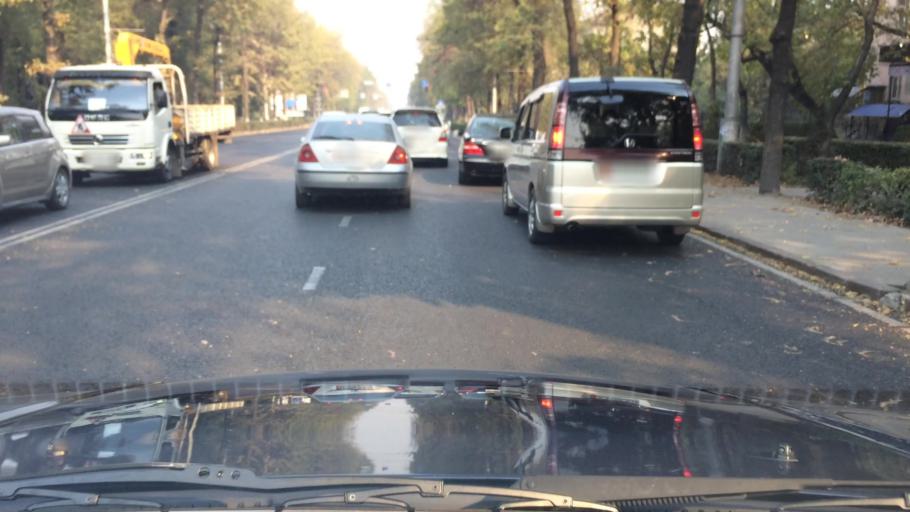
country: KG
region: Chuy
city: Bishkek
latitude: 42.8498
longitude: 74.5864
